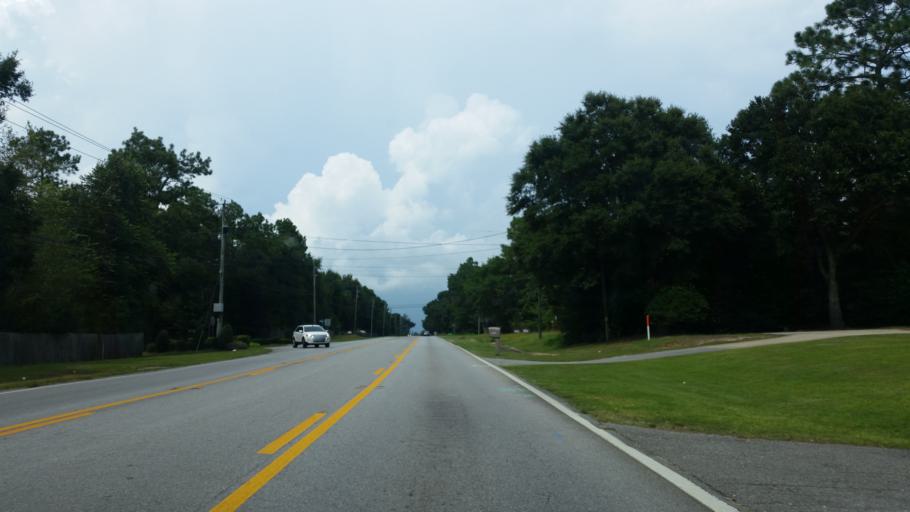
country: US
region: Florida
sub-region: Santa Rosa County
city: Pace
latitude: 30.6214
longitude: -87.1818
